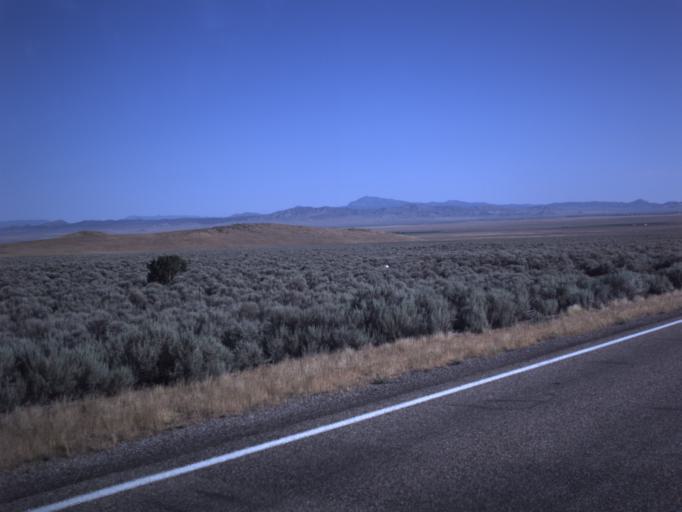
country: US
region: Utah
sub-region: Beaver County
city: Milford
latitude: 38.1403
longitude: -112.9600
